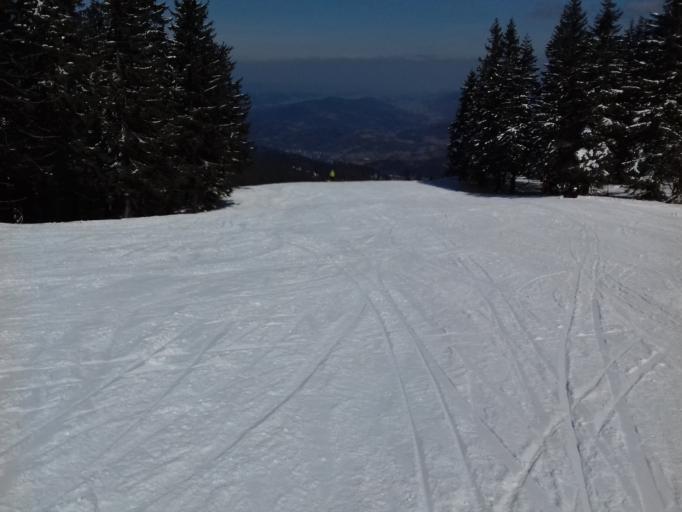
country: PL
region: Silesian Voivodeship
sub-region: Powiat zywiecki
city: Korbielow
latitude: 49.5381
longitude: 19.3195
